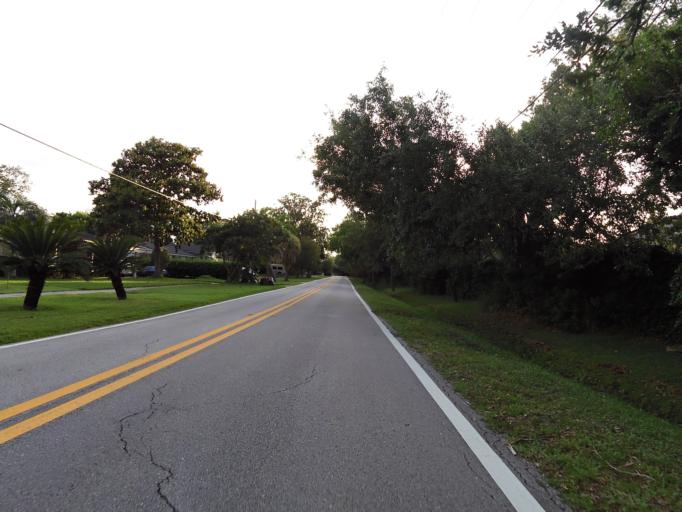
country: US
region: Florida
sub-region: Clay County
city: Orange Park
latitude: 30.2257
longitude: -81.6110
